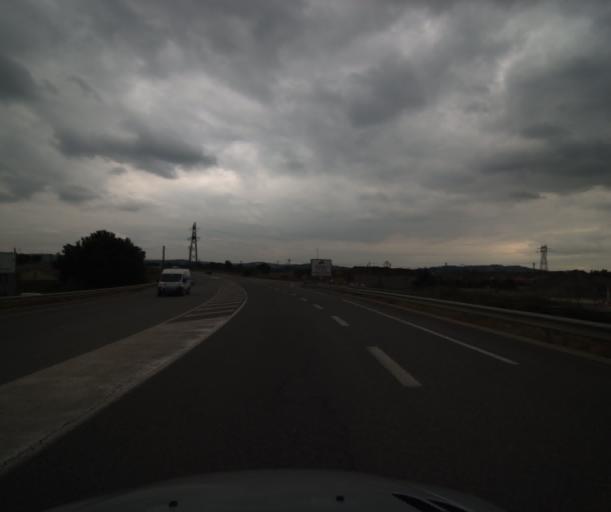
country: FR
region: Midi-Pyrenees
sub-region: Departement de la Haute-Garonne
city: Pinsaguel
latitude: 43.5244
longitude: 1.3832
